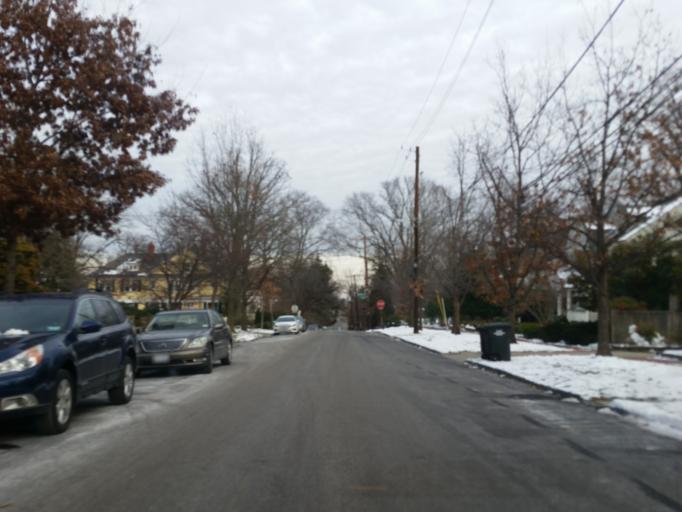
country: US
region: Maryland
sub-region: Montgomery County
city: Friendship Village
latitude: 38.9346
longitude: -77.0658
